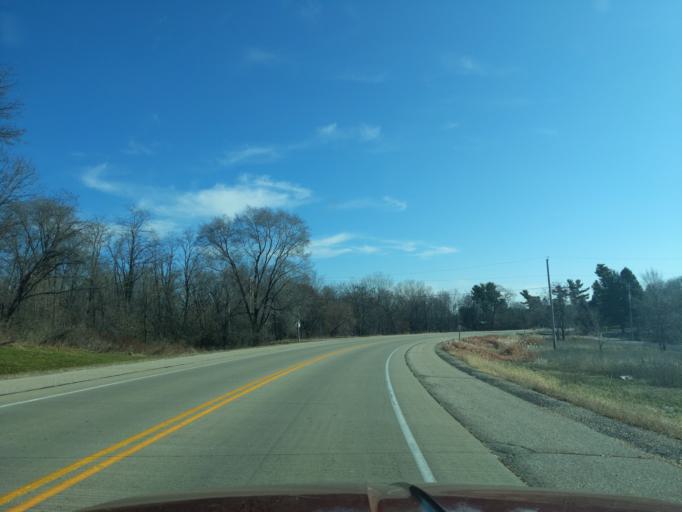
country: US
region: Wisconsin
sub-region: Waushara County
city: Silver Lake
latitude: 44.0632
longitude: -89.2427
